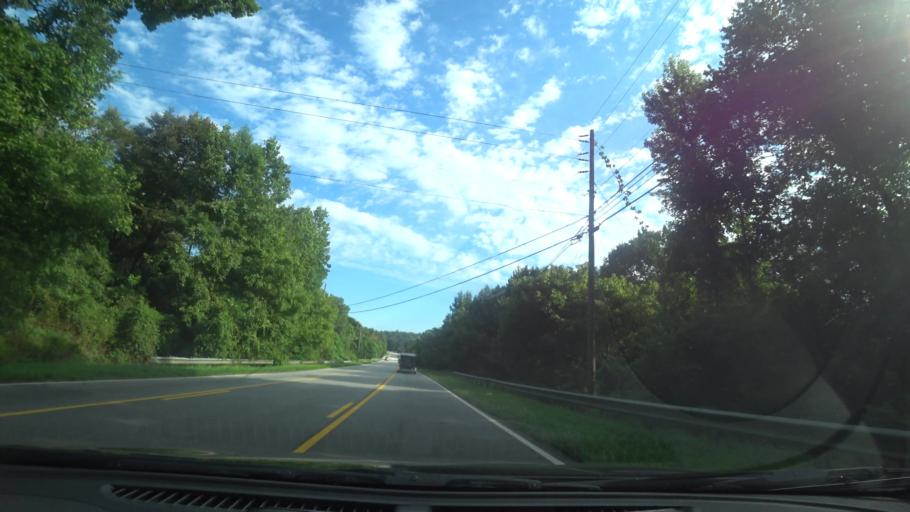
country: US
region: Georgia
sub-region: Rockdale County
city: Conyers
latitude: 33.6895
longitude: -83.9969
